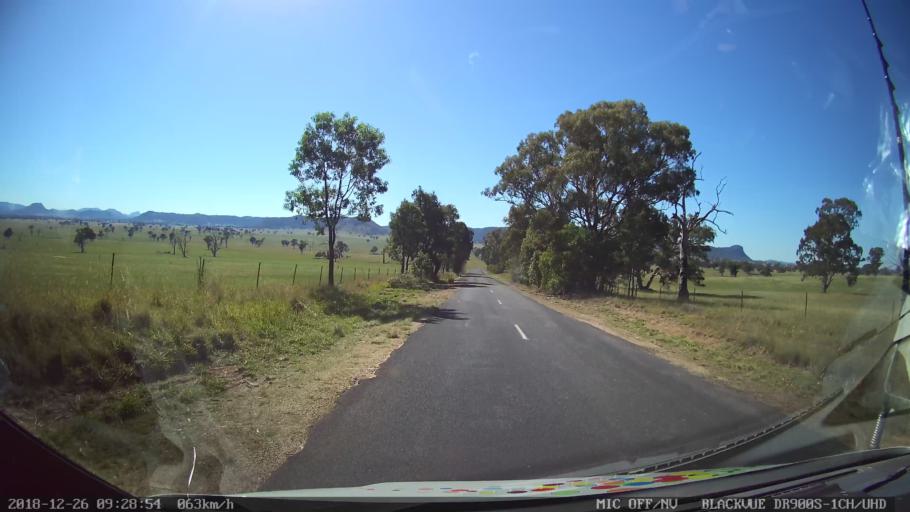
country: AU
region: New South Wales
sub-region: Mid-Western Regional
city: Kandos
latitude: -32.8488
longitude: 150.0238
